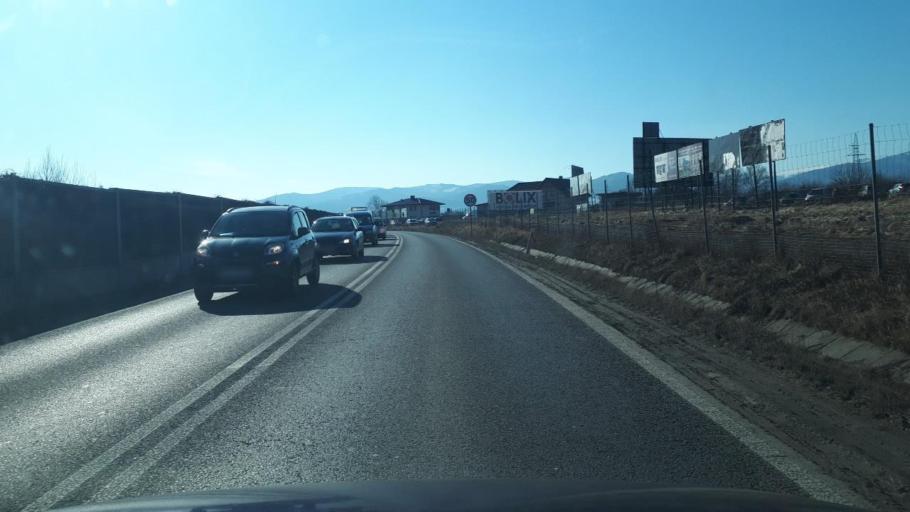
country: PL
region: Silesian Voivodeship
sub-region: Powiat zywiecki
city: Zywiec
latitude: 49.6893
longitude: 19.1772
